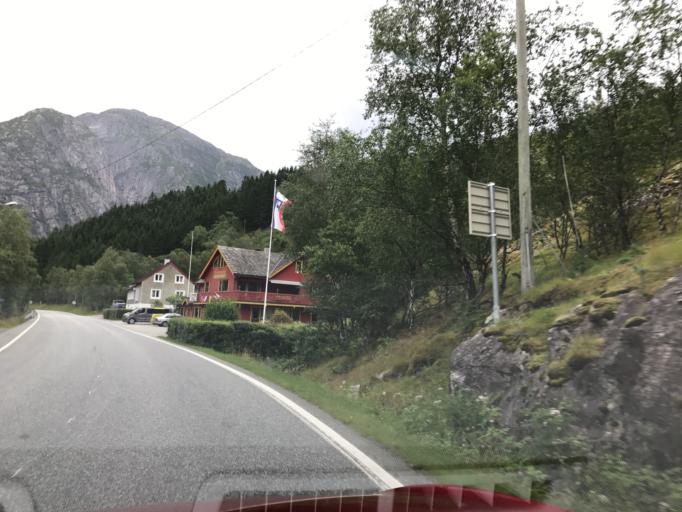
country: NO
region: Hordaland
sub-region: Eidfjord
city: Eidfjord
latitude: 60.4574
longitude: 7.0838
